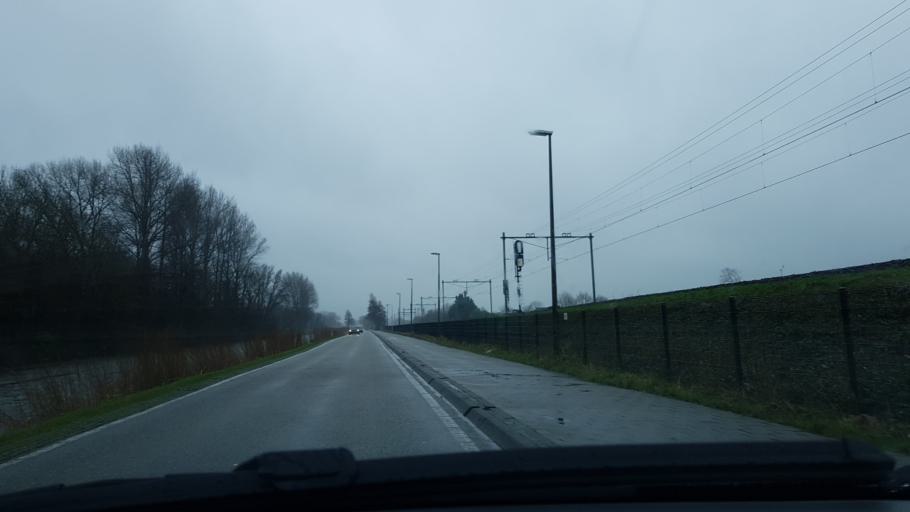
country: NL
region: North Holland
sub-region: Gemeente Heemstede
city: Heemstede
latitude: 52.3565
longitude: 4.6054
